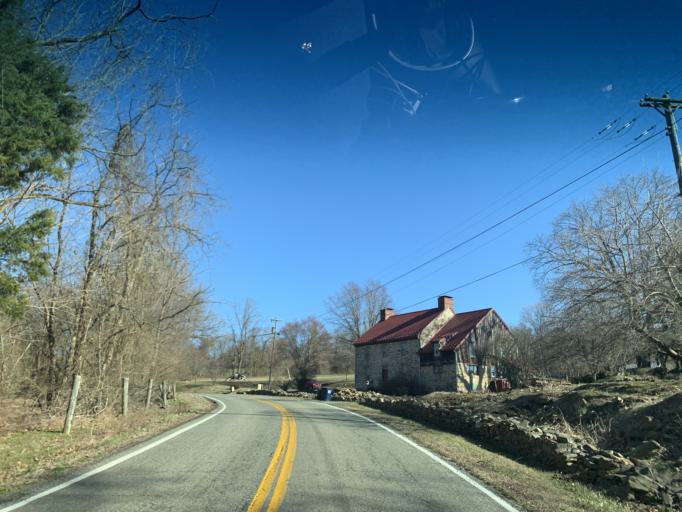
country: US
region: Maryland
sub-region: Cecil County
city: Rising Sun
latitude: 39.6870
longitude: -76.1125
